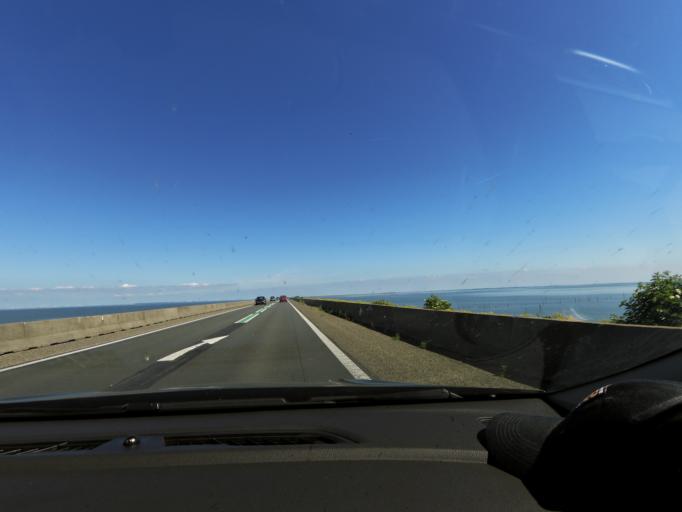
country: NL
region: North Holland
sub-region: Gemeente Enkhuizen
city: Enkhuizen
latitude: 52.6865
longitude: 5.3201
